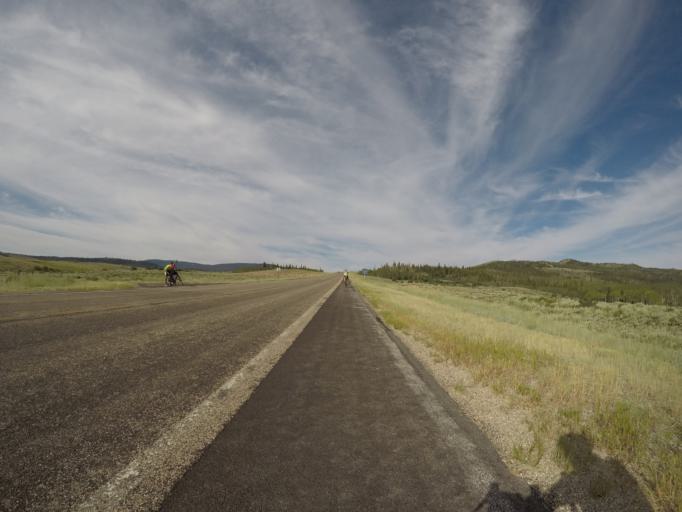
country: US
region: Wyoming
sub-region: Carbon County
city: Saratoga
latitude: 41.1857
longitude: -106.8598
